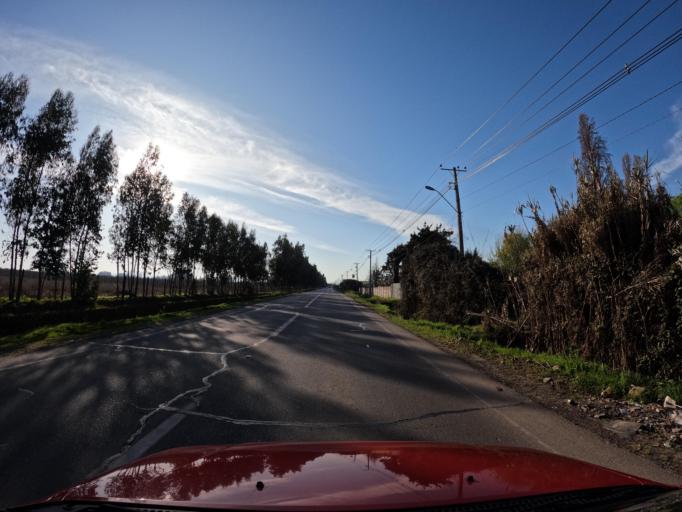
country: CL
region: Maule
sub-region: Provincia de Curico
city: Teno
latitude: -34.8779
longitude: -71.0812
